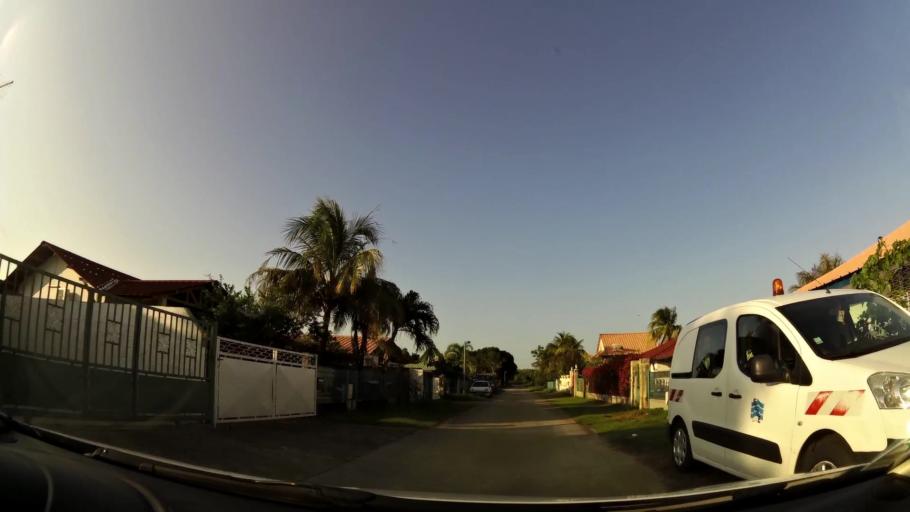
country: GF
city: Macouria
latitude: 5.0154
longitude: -52.4785
